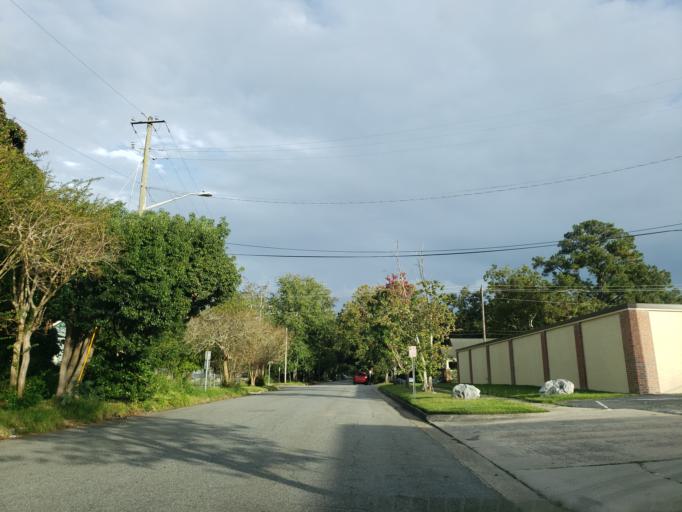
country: US
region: Georgia
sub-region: Chatham County
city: Savannah
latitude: 32.0623
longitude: -81.0878
